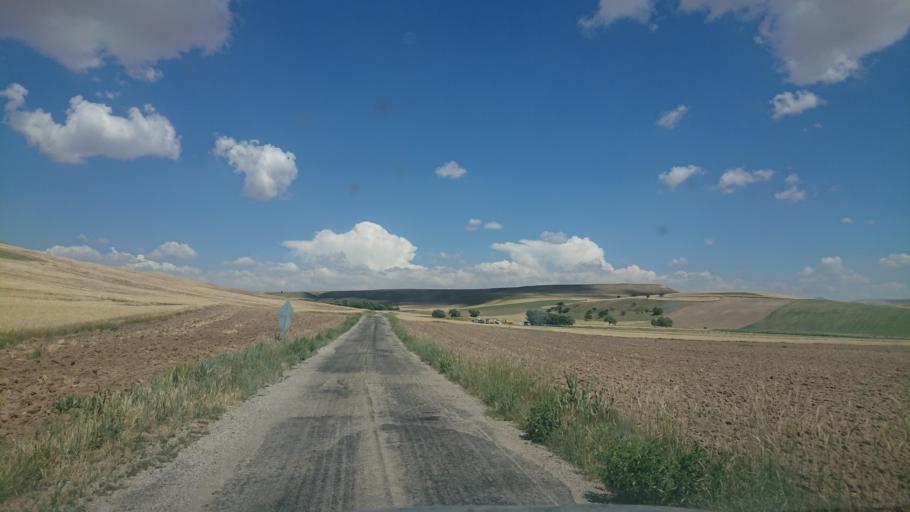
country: TR
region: Aksaray
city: Agacoren
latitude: 38.8001
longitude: 33.8195
